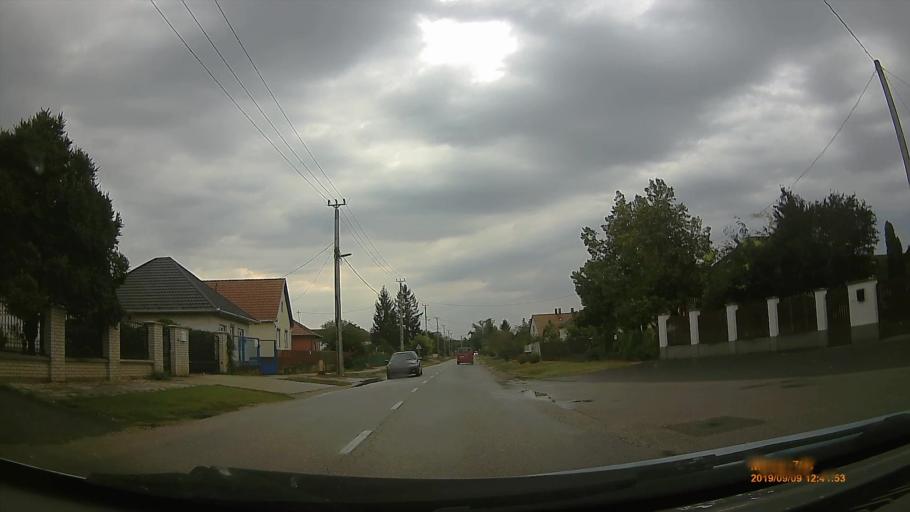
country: HU
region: Szabolcs-Szatmar-Bereg
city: Nyirpazony
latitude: 47.9773
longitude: 21.8019
